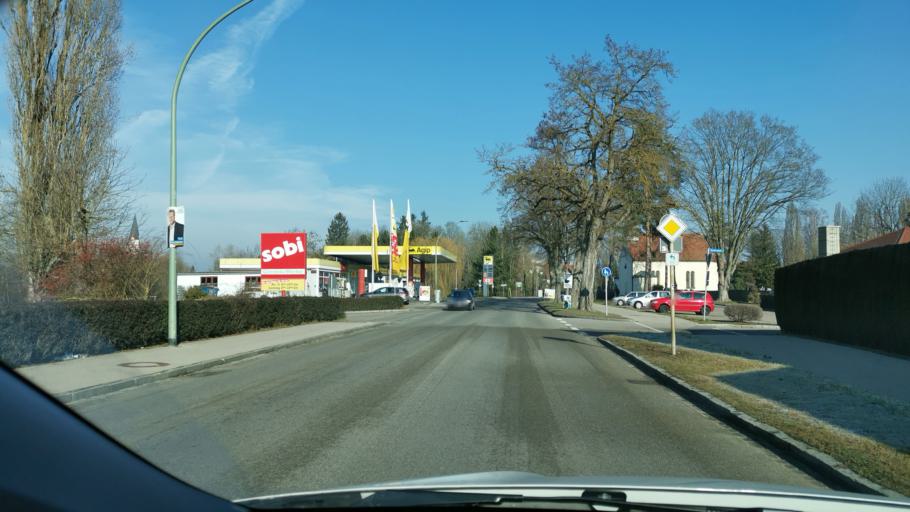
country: DE
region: Bavaria
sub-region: Swabia
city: Rain
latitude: 48.6866
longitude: 10.9198
